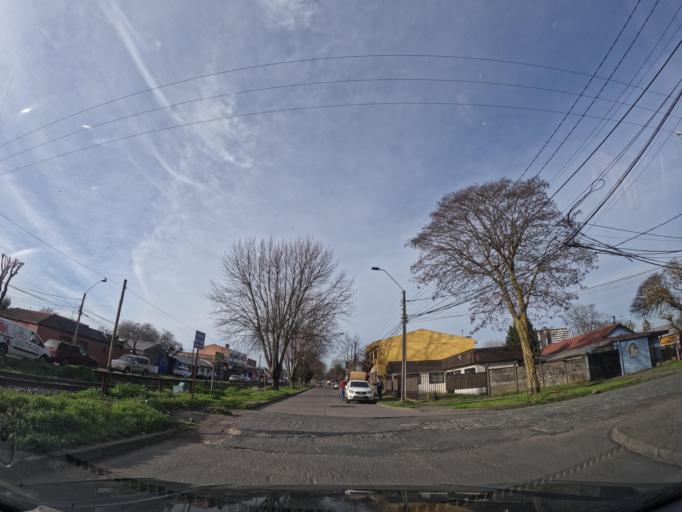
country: CL
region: Biobio
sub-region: Provincia de Concepcion
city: Concepcion
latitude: -36.8146
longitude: -73.0543
